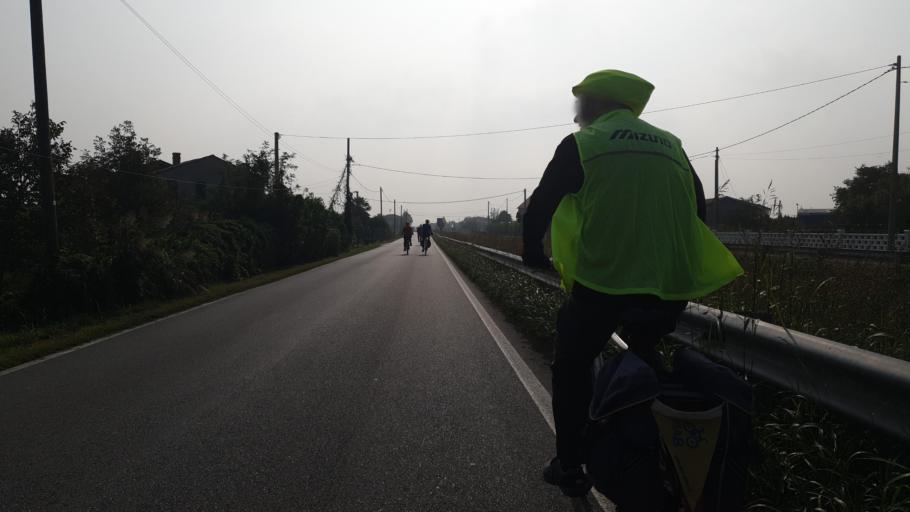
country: IT
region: Veneto
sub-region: Provincia di Padova
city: Corte
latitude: 45.2996
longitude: 12.0798
